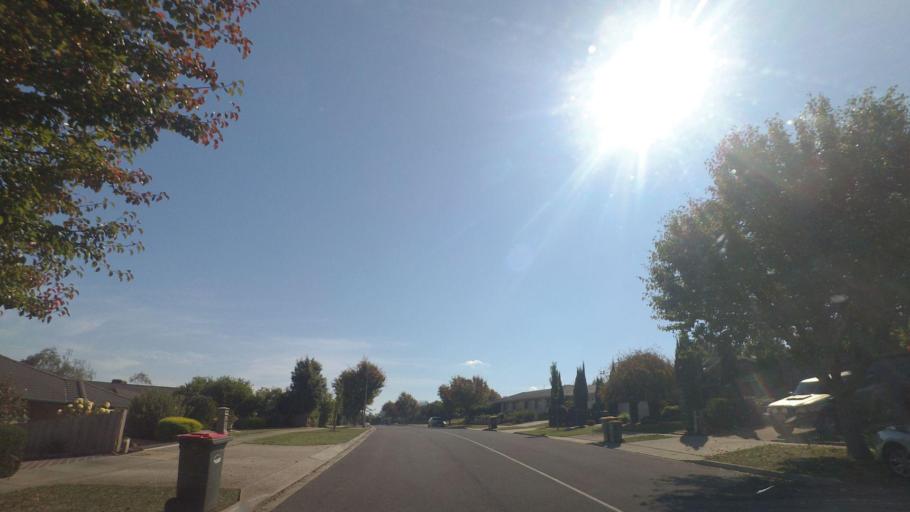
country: AU
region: Victoria
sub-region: Baw Baw
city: Warragul
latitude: -38.1495
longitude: 145.9485
